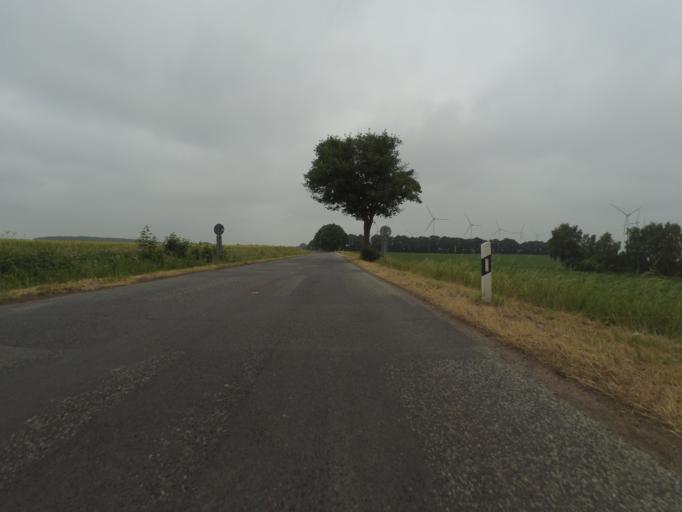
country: DE
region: Mecklenburg-Vorpommern
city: Plau am See
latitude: 53.4903
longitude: 12.2522
